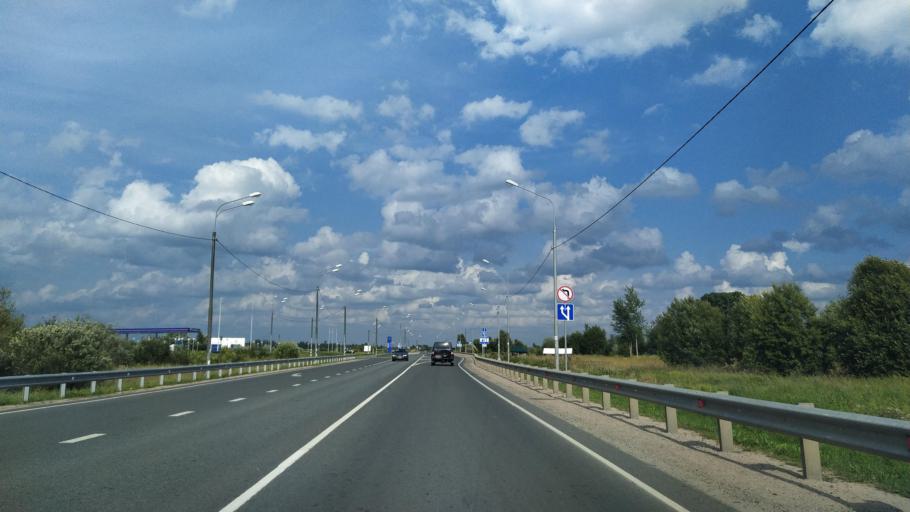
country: RU
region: Novgorod
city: Sol'tsy
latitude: 58.1281
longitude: 30.3567
